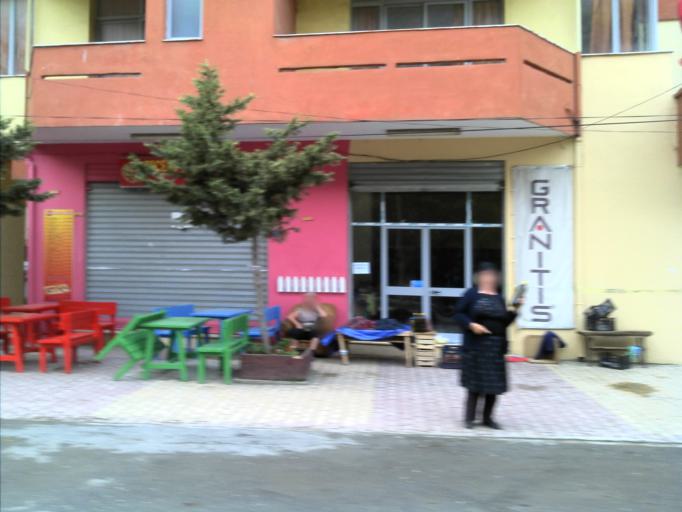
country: AL
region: Lezhe
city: Shengjin
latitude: 41.8094
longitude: 19.5998
